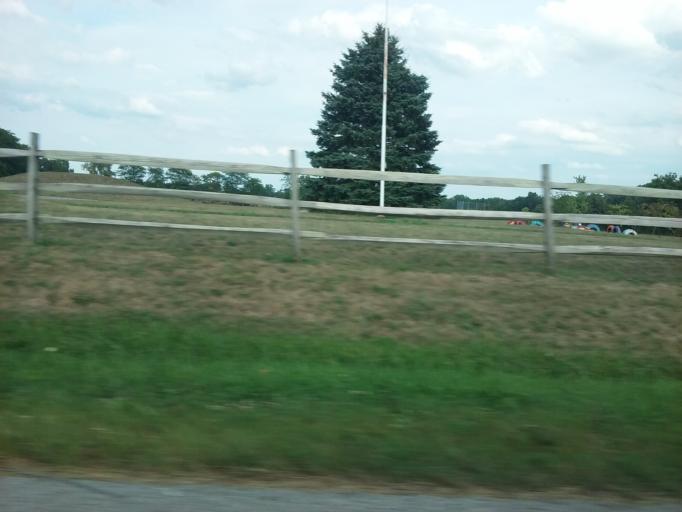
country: US
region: Ohio
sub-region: Wood County
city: Bowling Green
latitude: 41.3237
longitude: -83.6503
